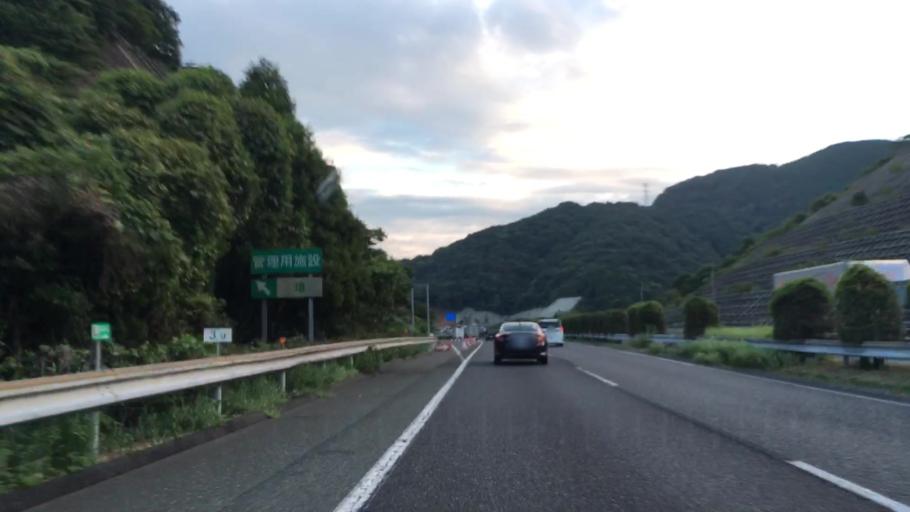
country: JP
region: Yamaguchi
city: Shimonoseki
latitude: 33.8922
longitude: 130.9711
